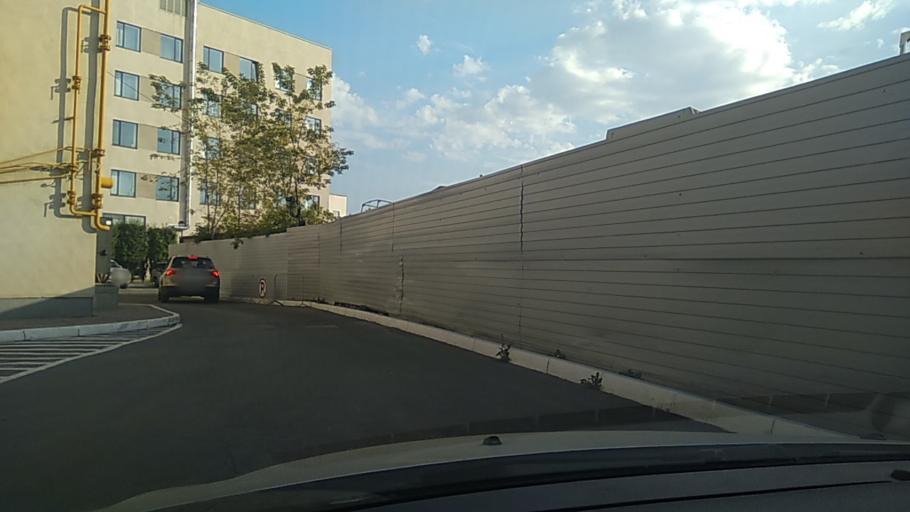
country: RU
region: Sverdlovsk
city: Yekaterinburg
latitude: 56.8187
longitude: 60.6518
